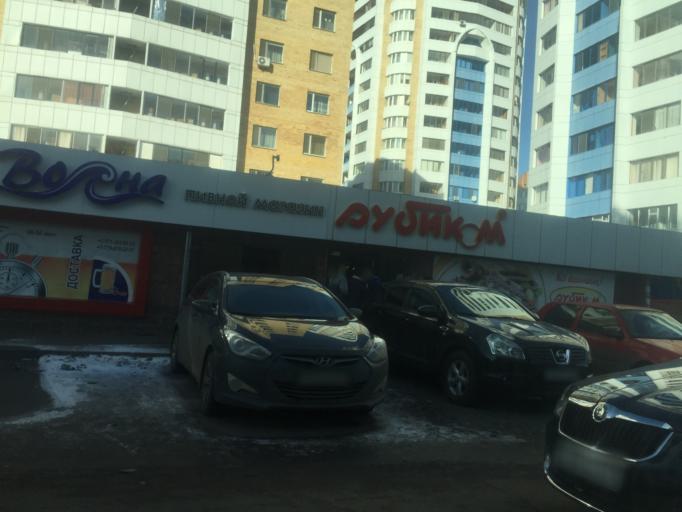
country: KZ
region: Astana Qalasy
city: Astana
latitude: 51.1616
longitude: 71.4346
